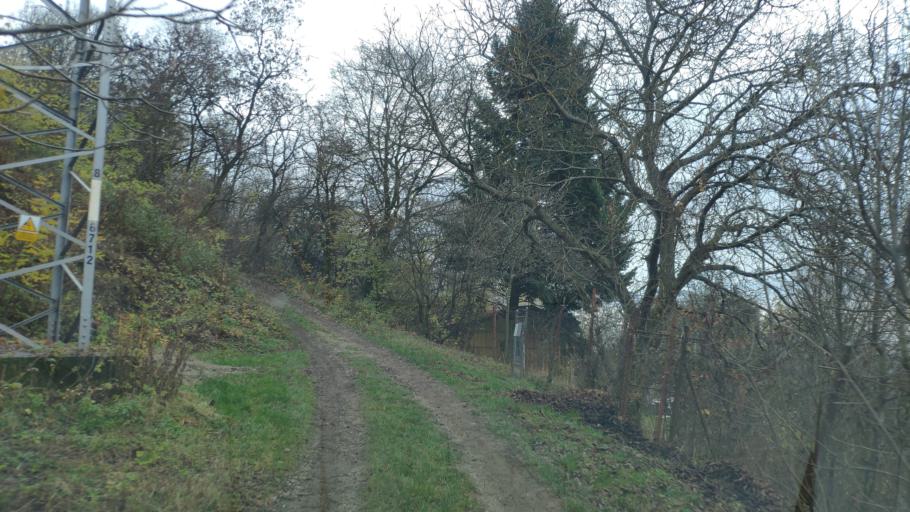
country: SK
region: Kosicky
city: Kosice
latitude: 48.6962
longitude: 21.2916
